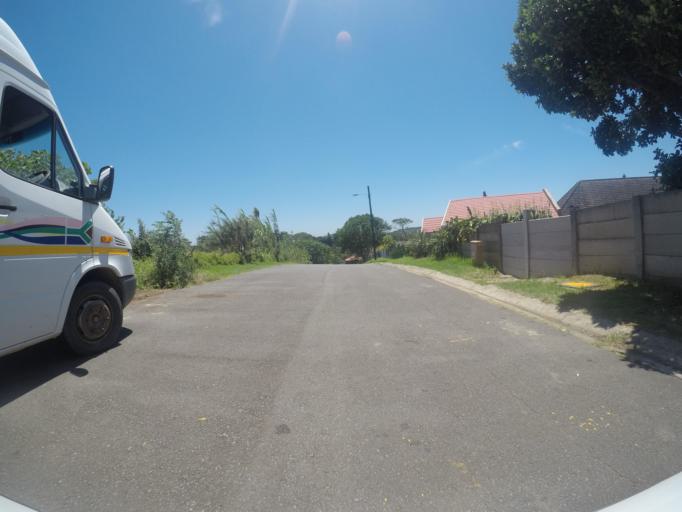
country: ZA
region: Eastern Cape
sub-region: Buffalo City Metropolitan Municipality
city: East London
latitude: -32.9366
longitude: 28.0066
